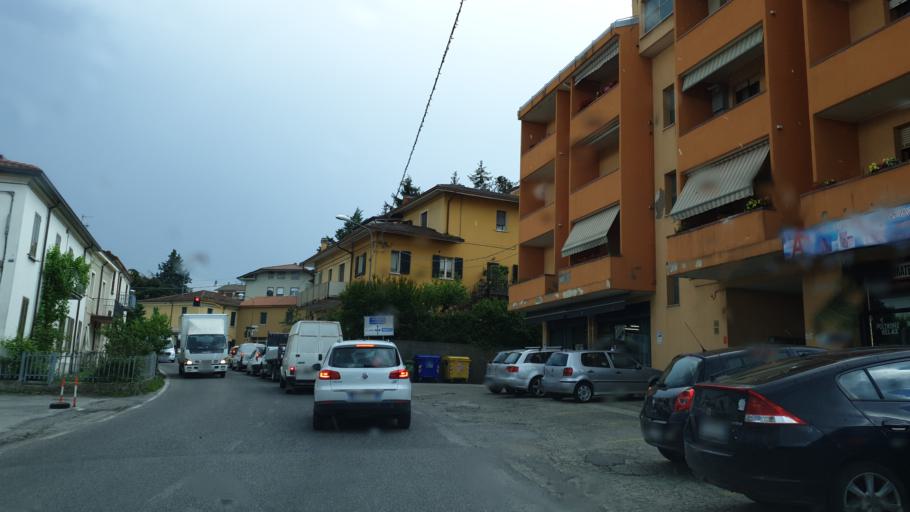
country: IT
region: Emilia-Romagna
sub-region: Provincia di Rimini
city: Novafeltria
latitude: 43.8987
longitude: 12.2890
